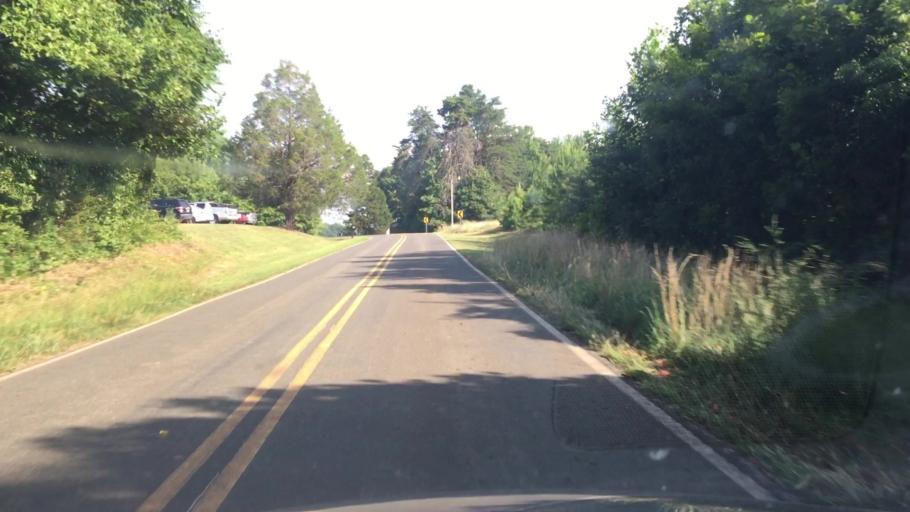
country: US
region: North Carolina
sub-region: Rockingham County
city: Reidsville
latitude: 36.2717
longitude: -79.5661
